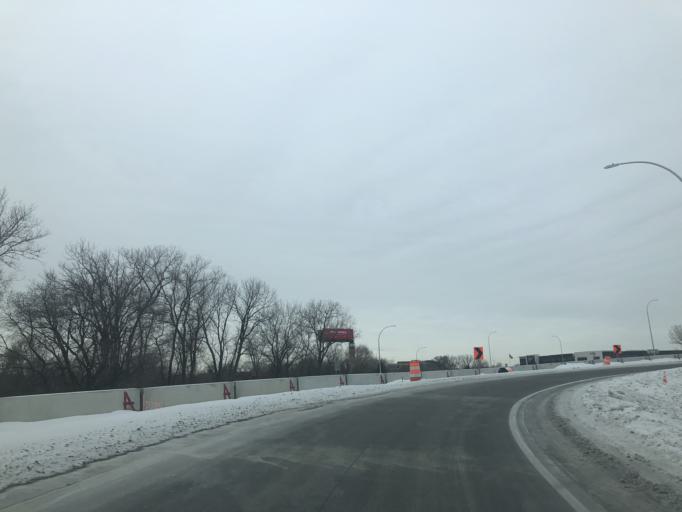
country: US
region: Minnesota
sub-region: Ramsey County
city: New Brighton
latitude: 45.0659
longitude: -93.1874
